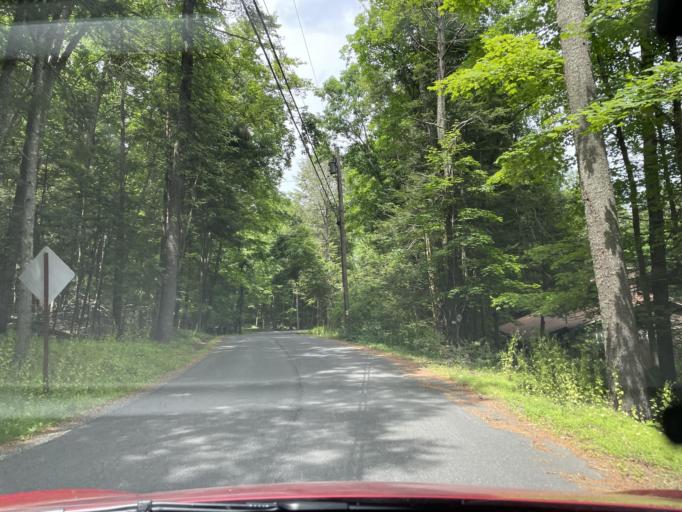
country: US
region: New York
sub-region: Ulster County
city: Zena
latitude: 41.9893
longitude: -74.0610
